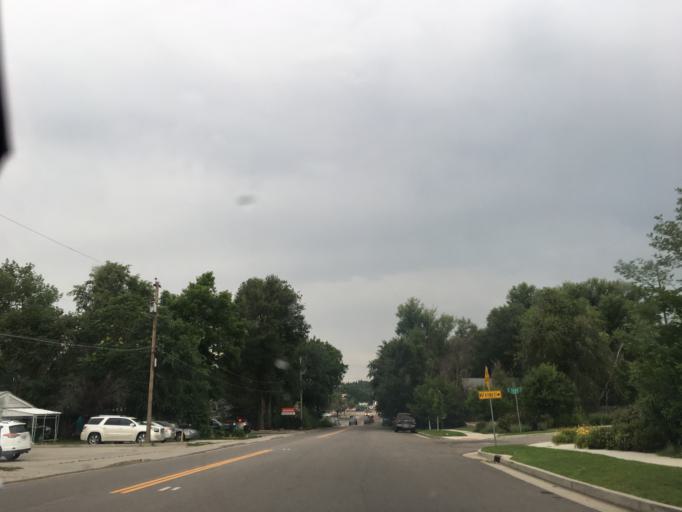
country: US
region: Colorado
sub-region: Arapahoe County
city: Sheridan
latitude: 39.6560
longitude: -105.0322
